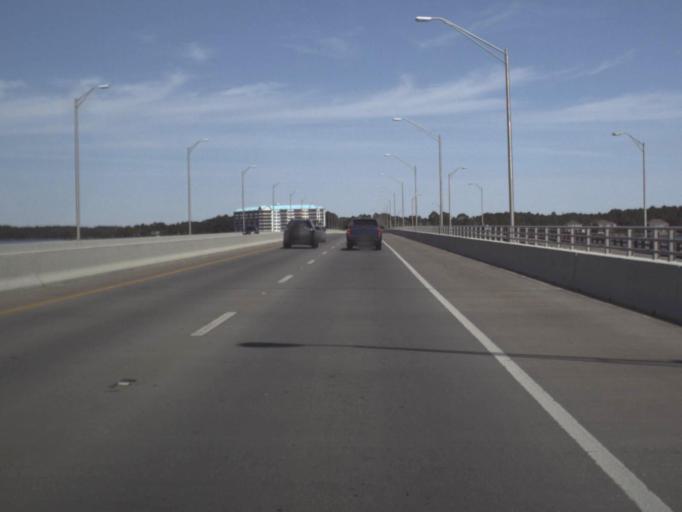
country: US
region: Florida
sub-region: Bay County
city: Lynn Haven
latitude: 30.2568
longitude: -85.6470
